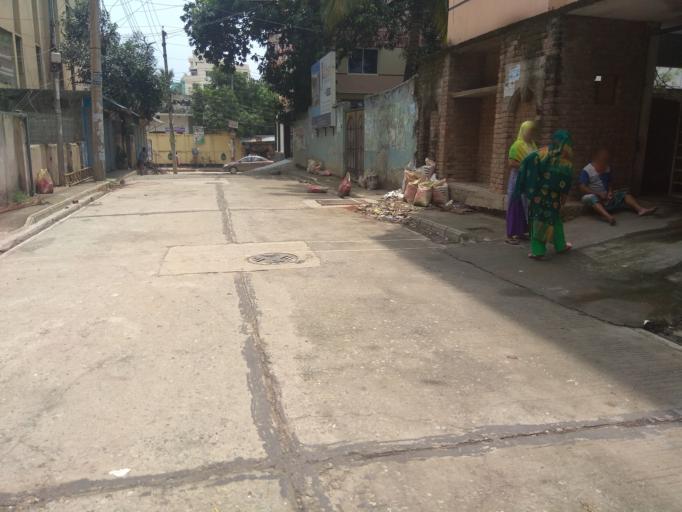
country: BD
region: Dhaka
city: Azimpur
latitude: 23.8066
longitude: 90.3572
